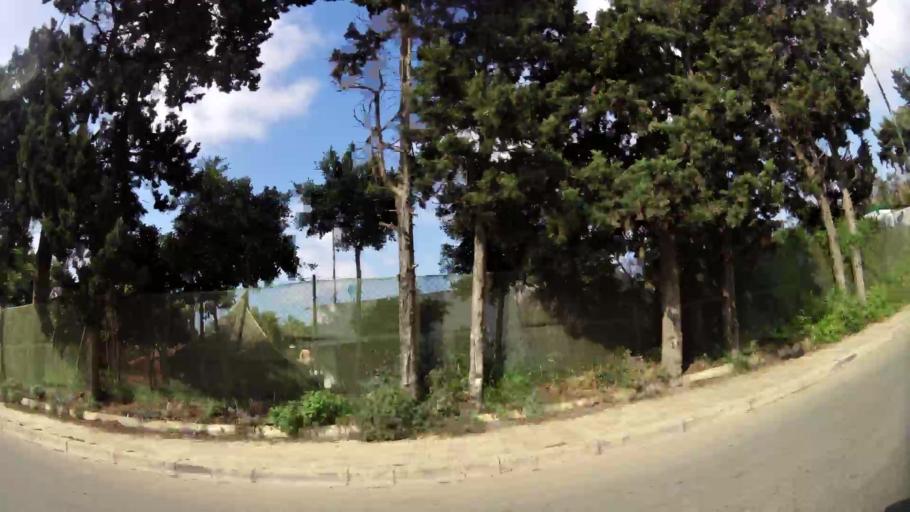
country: MA
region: Rabat-Sale-Zemmour-Zaer
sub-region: Rabat
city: Rabat
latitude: 33.9733
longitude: -6.8612
